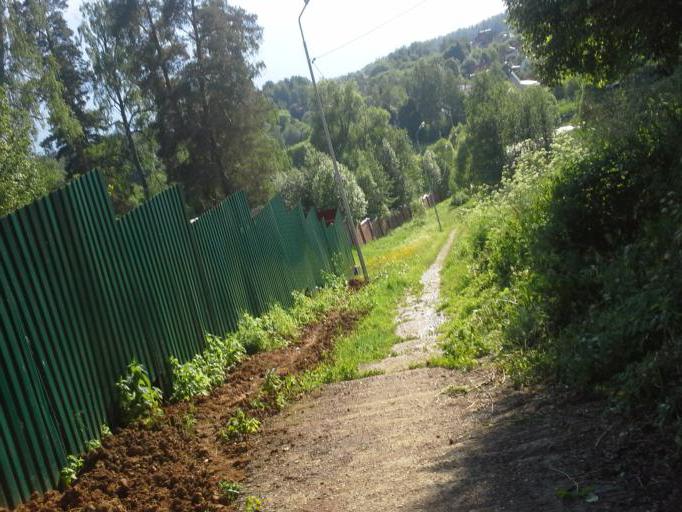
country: RU
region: Moskovskaya
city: Filimonki
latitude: 55.5751
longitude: 37.3494
